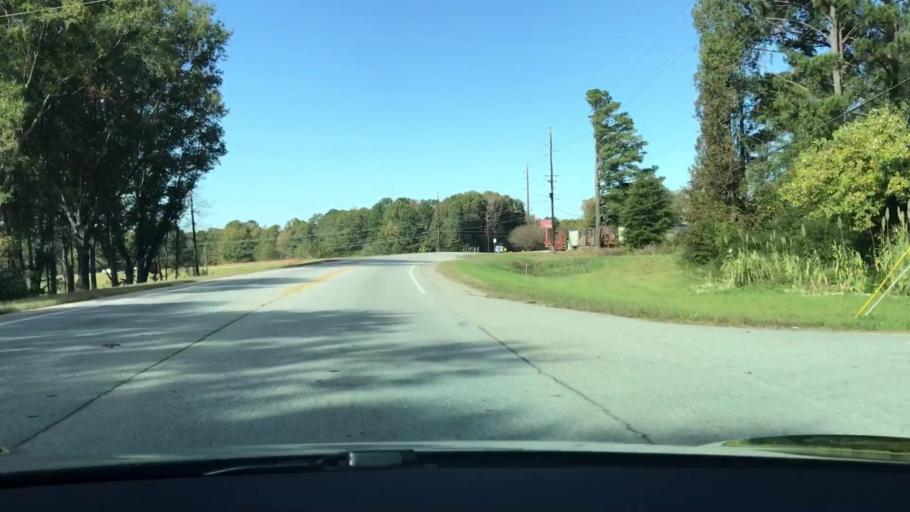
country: US
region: Georgia
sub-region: Warren County
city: Warrenton
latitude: 33.4005
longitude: -82.6660
